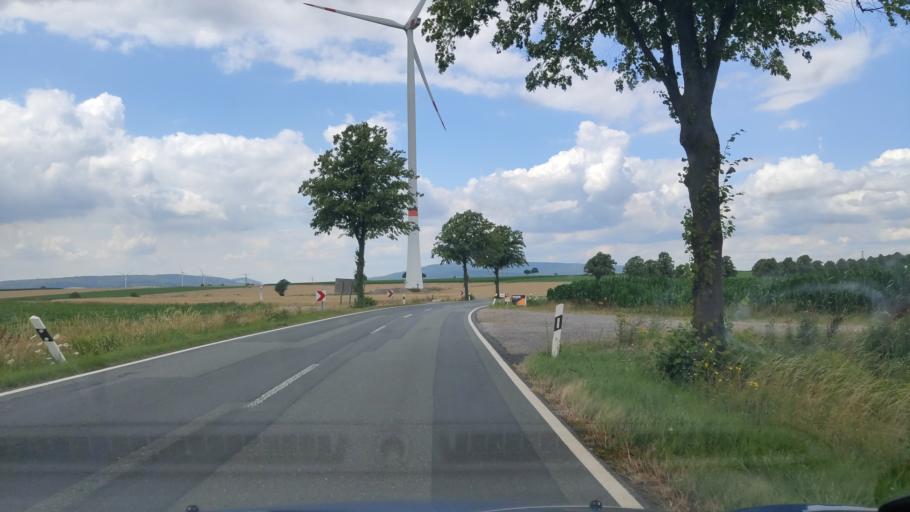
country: DE
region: Lower Saxony
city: Coppenbrugge
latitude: 52.1253
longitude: 9.5009
